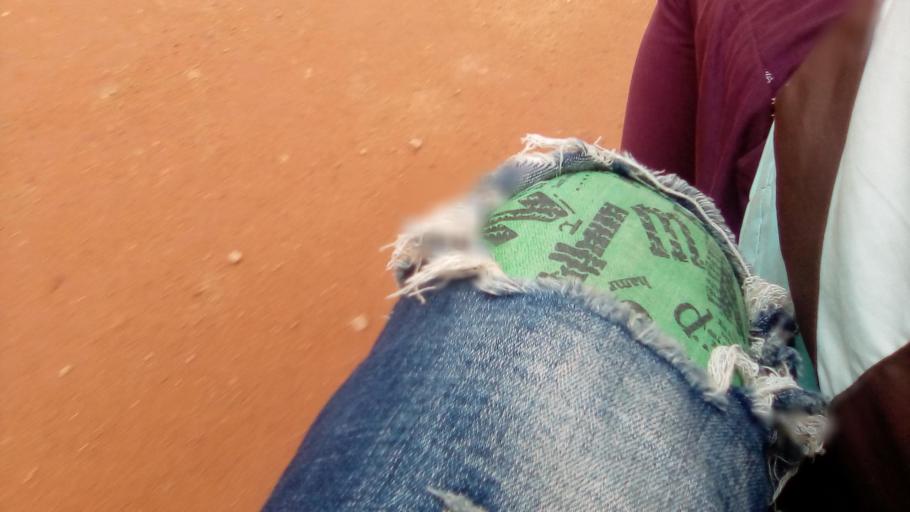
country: SL
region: Southern Province
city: Pujehun
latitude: 7.3738
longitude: -11.7123
